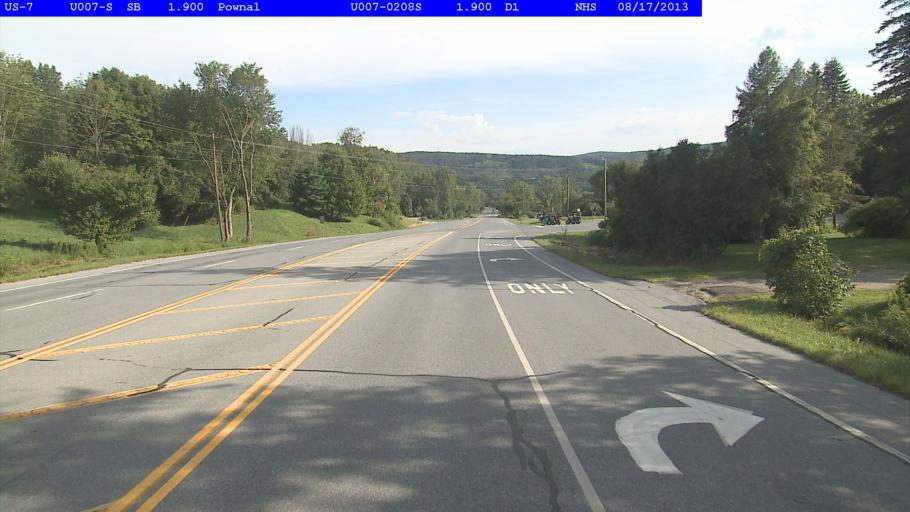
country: US
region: Massachusetts
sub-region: Berkshire County
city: Williamstown
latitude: 42.7642
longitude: -73.2324
